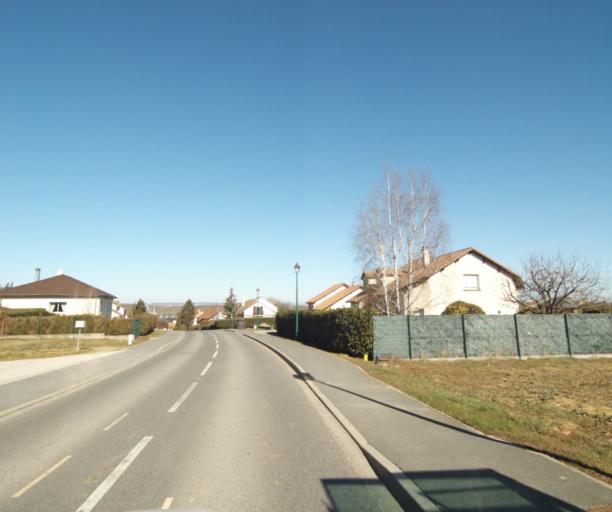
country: FR
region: Lorraine
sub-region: Departement de Meurthe-et-Moselle
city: Fleville-devant-Nancy
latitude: 48.6216
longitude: 6.2023
